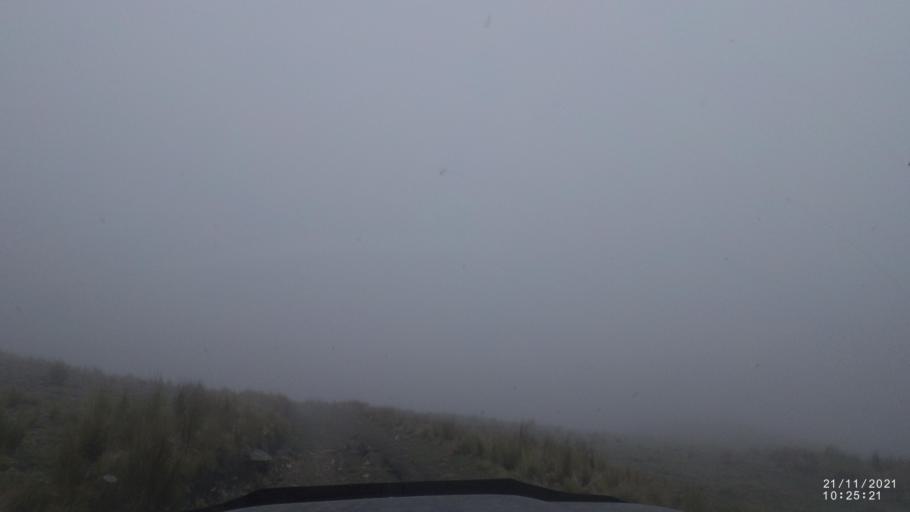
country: BO
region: Cochabamba
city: Cochabamba
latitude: -16.9764
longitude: -66.2641
